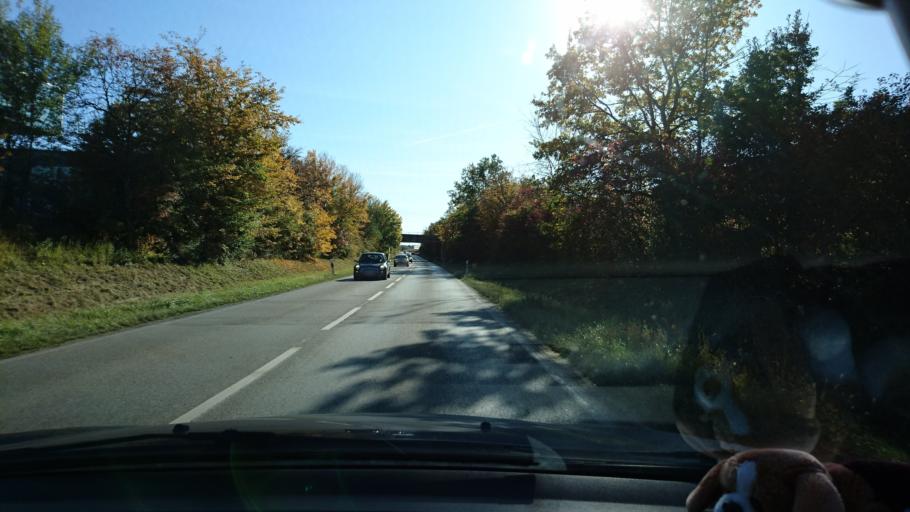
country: DE
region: Bavaria
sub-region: Upper Bavaria
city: Zorneding
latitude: 48.0932
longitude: 11.8207
